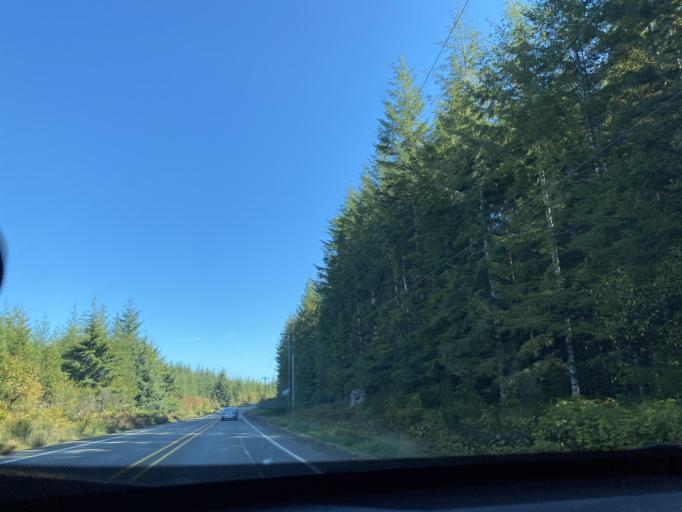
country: US
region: Washington
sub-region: Clallam County
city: Forks
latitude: 47.9534
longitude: -124.4587
